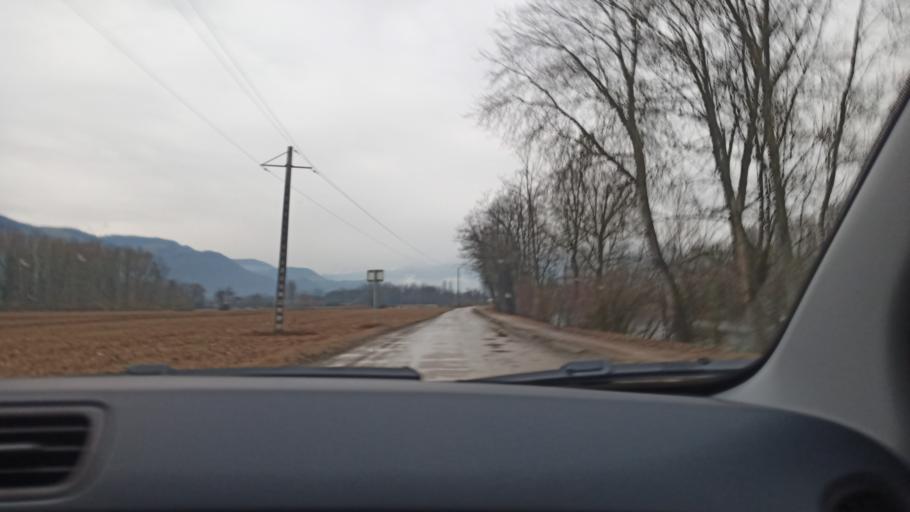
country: FR
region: Rhone-Alpes
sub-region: Departement de l'Isere
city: Domene
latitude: 45.2176
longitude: 5.8397
